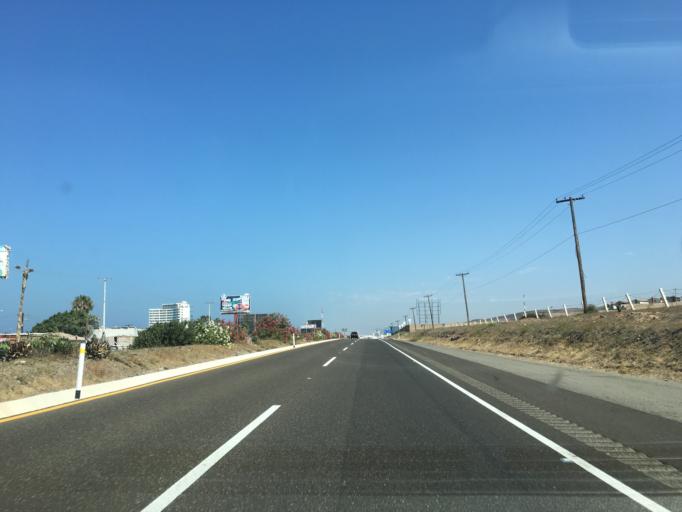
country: MX
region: Baja California
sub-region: Playas de Rosarito
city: Ciudad Morelos
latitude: 32.2960
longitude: -117.0382
